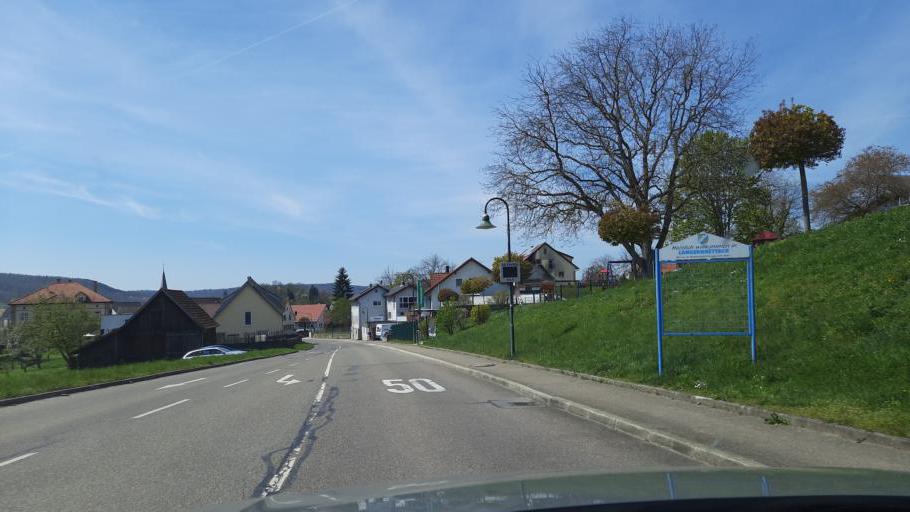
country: DE
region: Baden-Wuerttemberg
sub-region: Regierungsbezirk Stuttgart
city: Neuenstadt am Kocher
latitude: 49.2273
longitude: 9.3833
